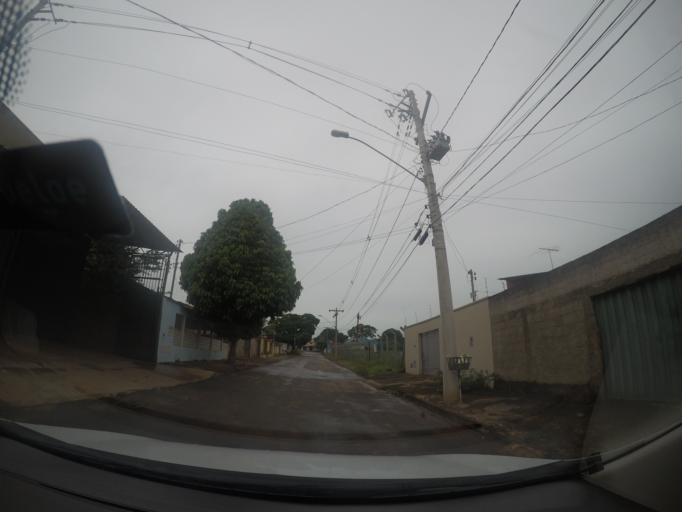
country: BR
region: Goias
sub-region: Goiania
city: Goiania
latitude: -16.6252
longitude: -49.2340
